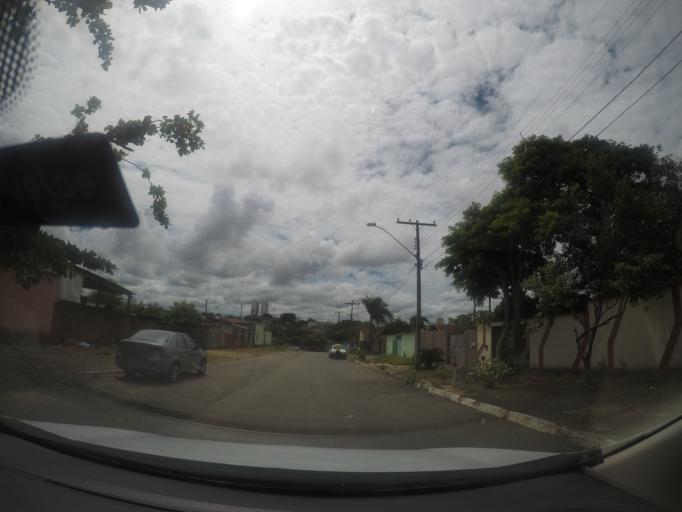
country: BR
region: Goias
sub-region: Goiania
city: Goiania
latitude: -16.6645
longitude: -49.3001
